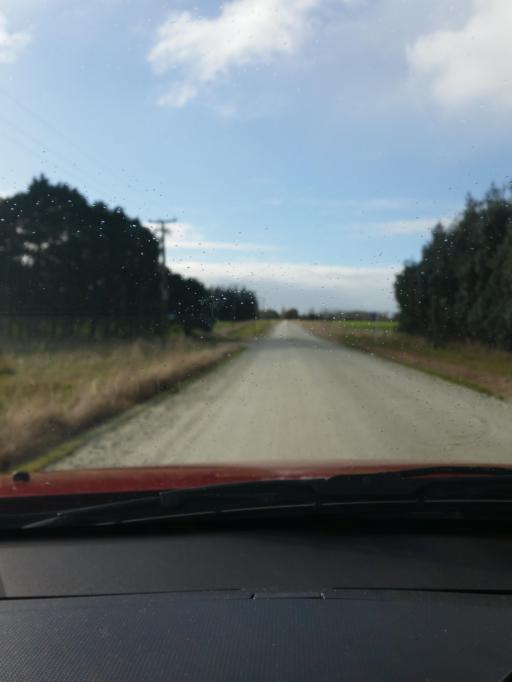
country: NZ
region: Southland
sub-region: Invercargill City
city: Invercargill
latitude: -46.3712
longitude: 168.6352
